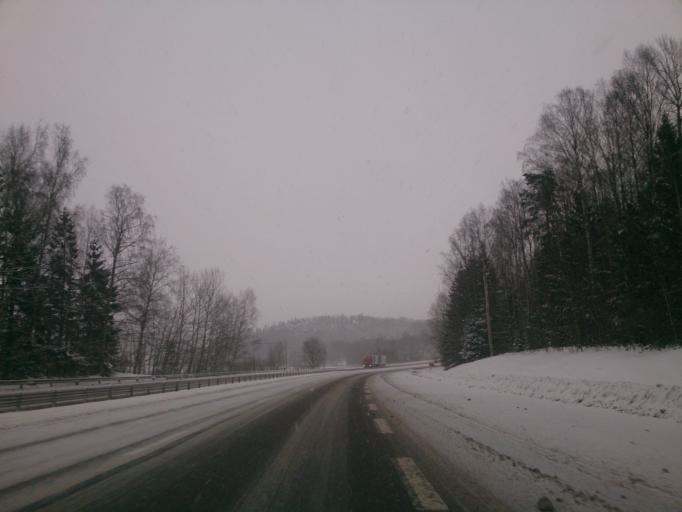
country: SE
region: Soedermanland
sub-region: Nykopings Kommun
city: Nykoping
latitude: 58.7666
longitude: 16.9938
